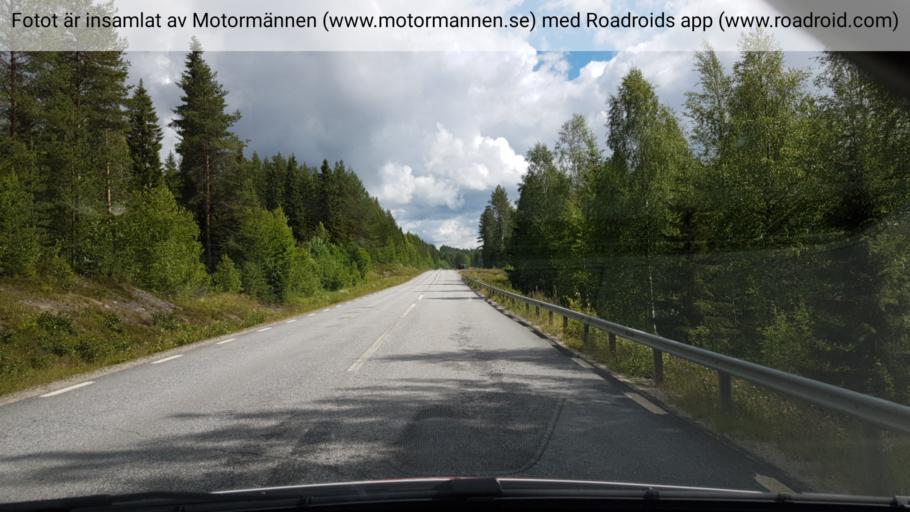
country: SE
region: Vaesterbotten
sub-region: Bjurholms Kommun
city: Bjurholm
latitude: 64.2782
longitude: 19.2482
